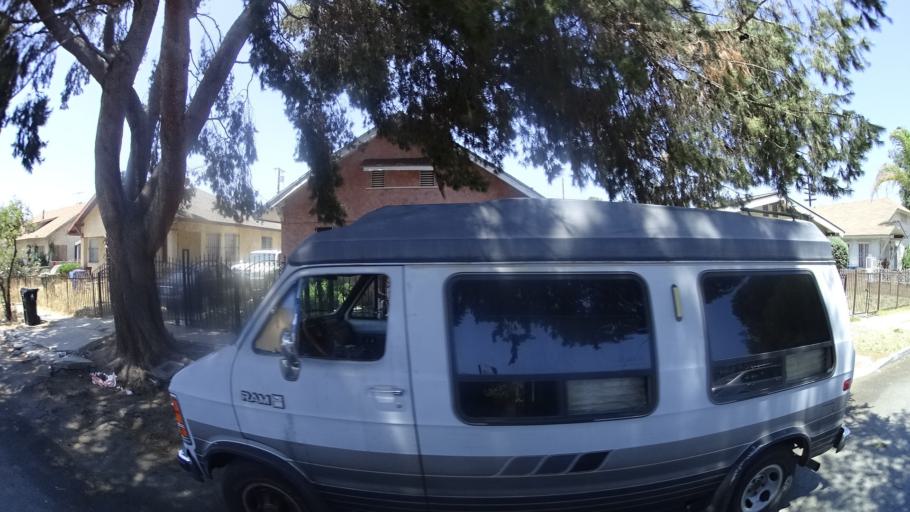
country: US
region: California
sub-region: Los Angeles County
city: View Park-Windsor Hills
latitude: 34.0028
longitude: -118.3100
